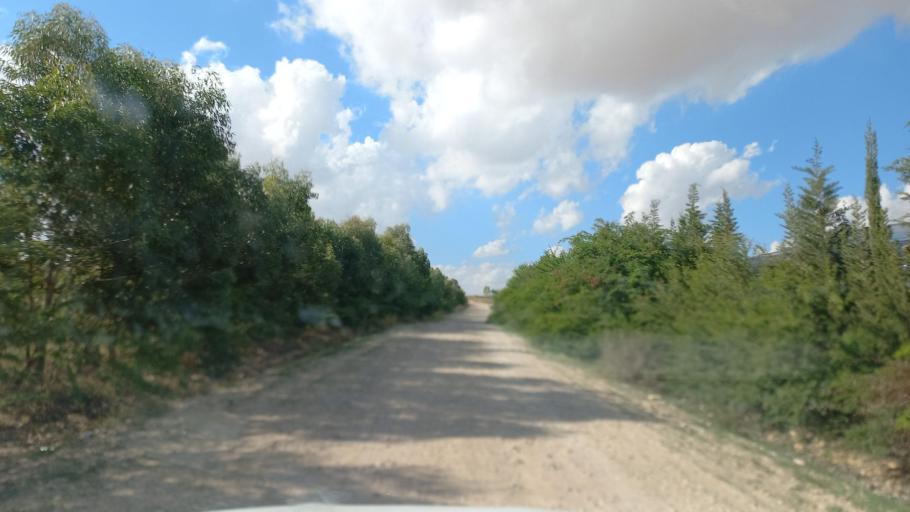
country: TN
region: Al Qasrayn
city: Sbiba
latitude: 35.3394
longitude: 9.0773
